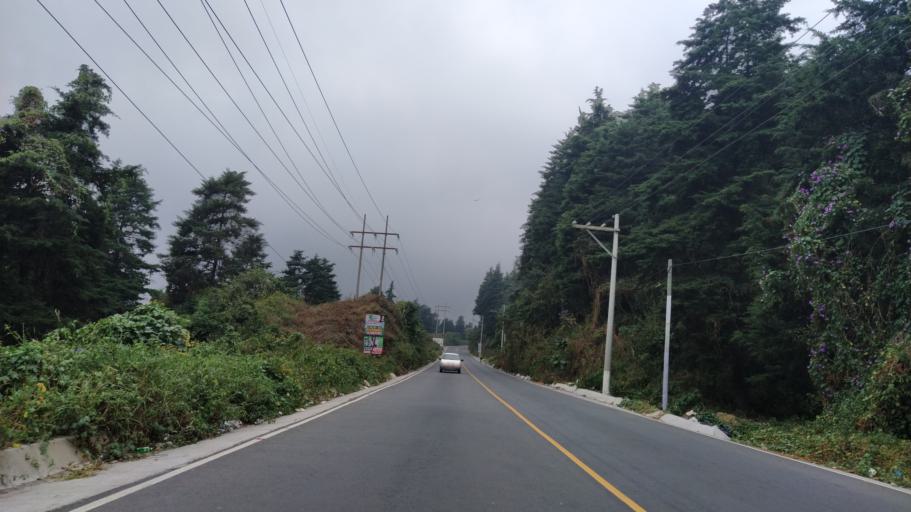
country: GT
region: Quetzaltenango
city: Zunil
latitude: 14.7421
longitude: -91.5155
